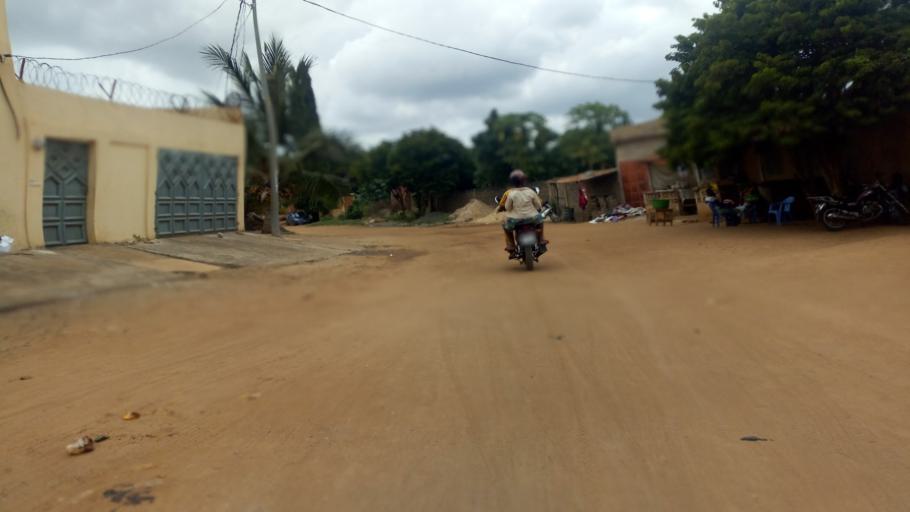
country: TG
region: Maritime
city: Lome
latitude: 6.2269
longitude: 1.1877
